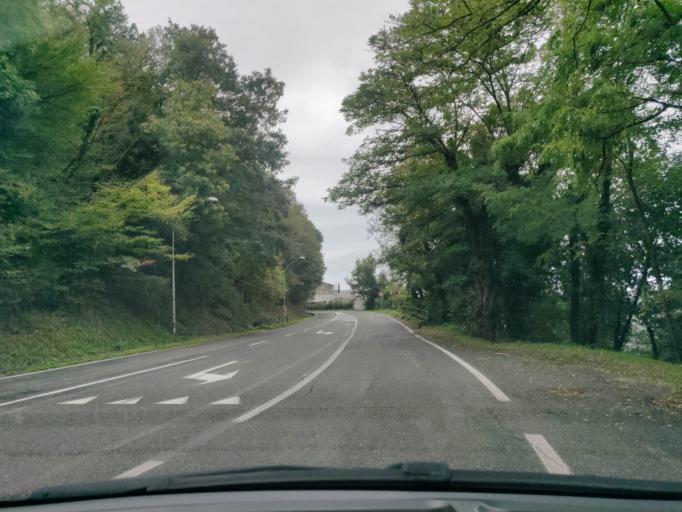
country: IT
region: Latium
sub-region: Citta metropolitana di Roma Capitale
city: Allumiere
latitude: 42.1538
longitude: 11.9018
